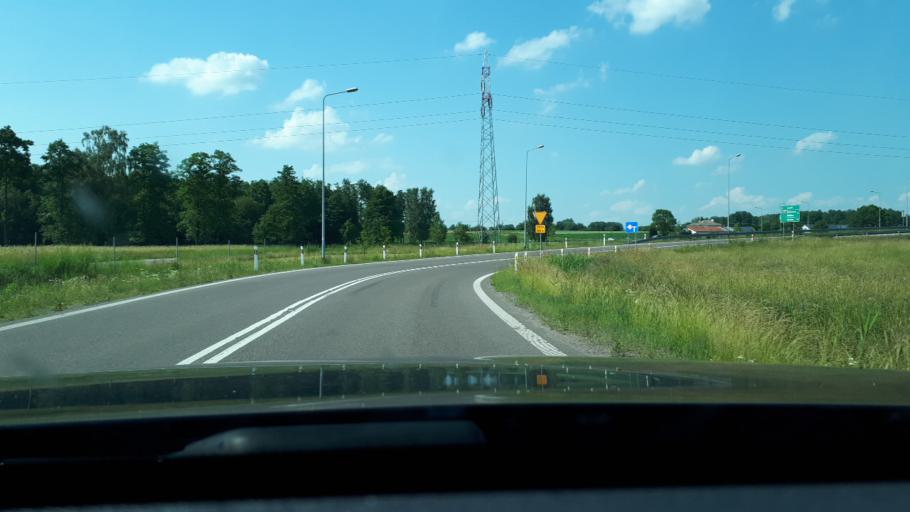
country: PL
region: Podlasie
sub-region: Powiat bialostocki
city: Tykocin
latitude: 53.1558
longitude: 22.8638
